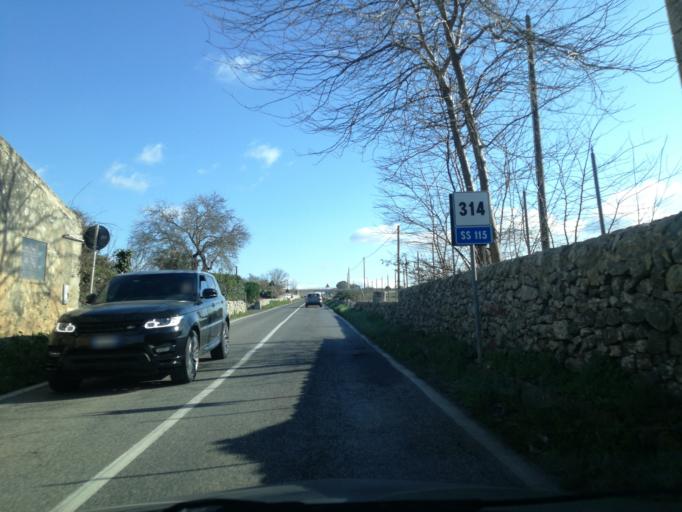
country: IT
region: Sicily
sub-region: Ragusa
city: Comiso
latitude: 36.9399
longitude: 14.6453
